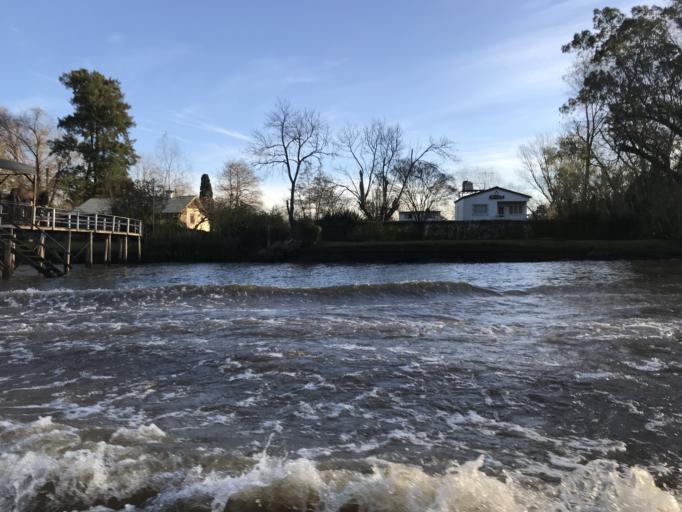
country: AR
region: Buenos Aires
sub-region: Partido de Tigre
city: Tigre
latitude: -34.3934
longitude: -58.5732
